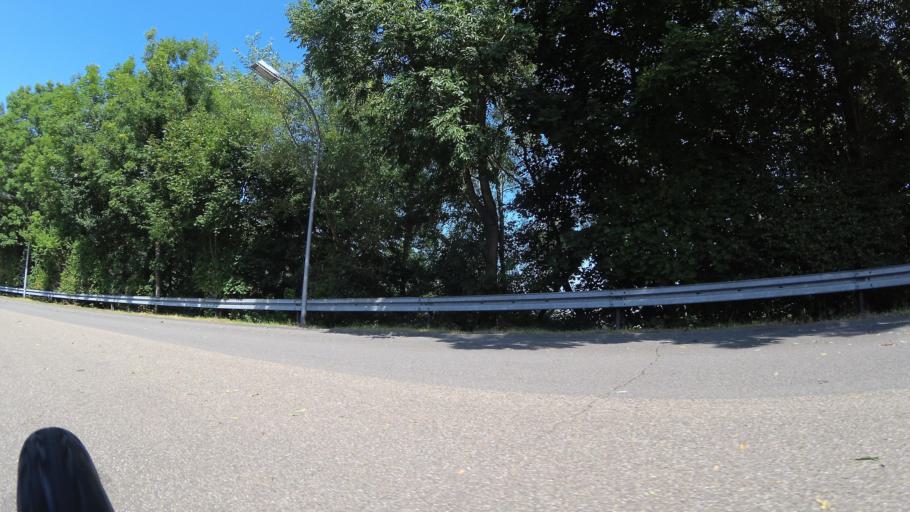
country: DE
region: Saarland
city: Saarbrucken
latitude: 49.2305
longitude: 6.9860
